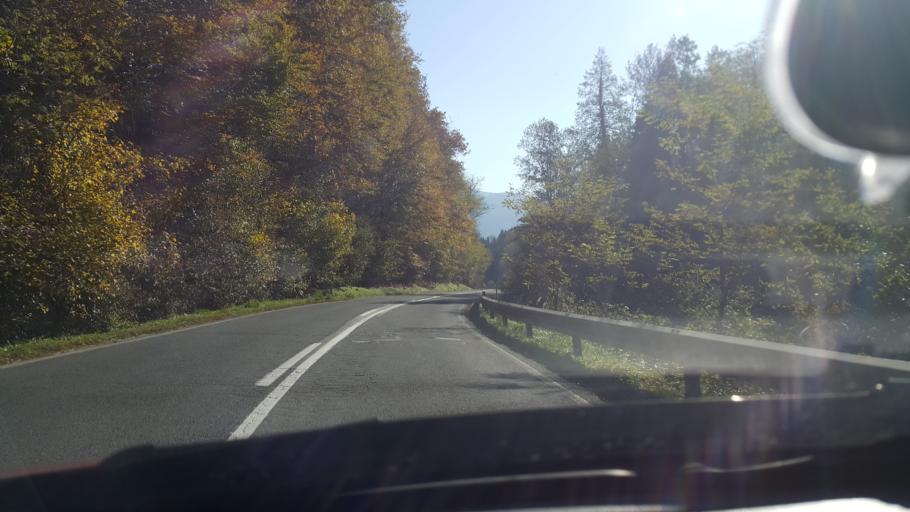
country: SI
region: Bistrica ob Sotli
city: Bistrica ob Sotli
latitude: 46.0721
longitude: 15.6433
